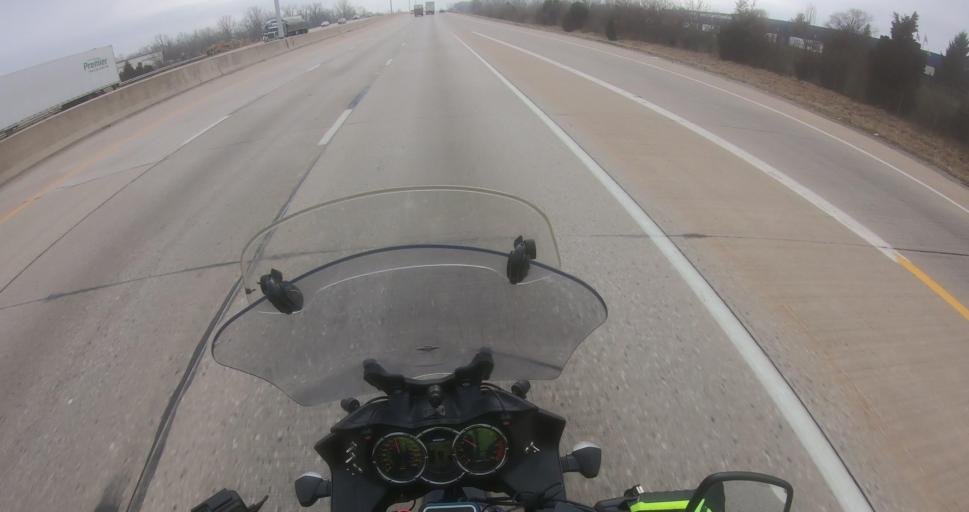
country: US
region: Ohio
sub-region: Miami County
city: Troy
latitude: 40.0212
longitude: -84.2308
